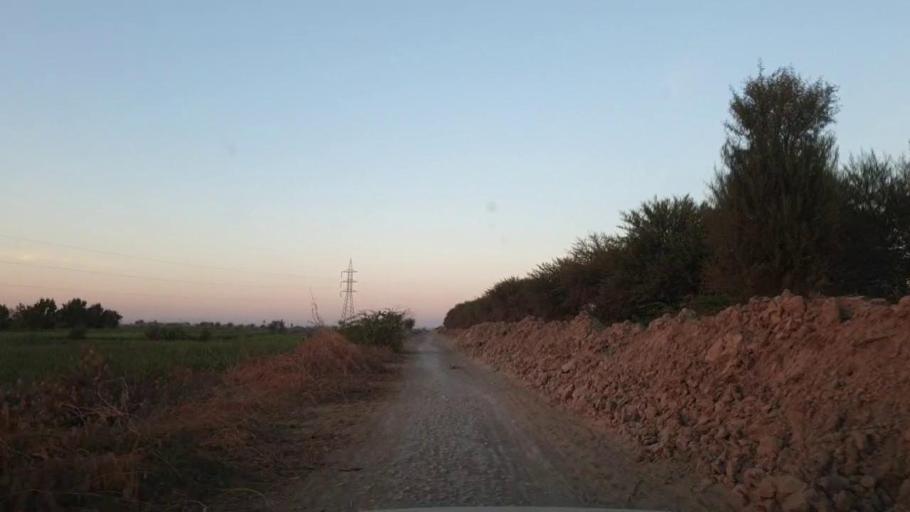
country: PK
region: Sindh
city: Kunri
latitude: 25.1512
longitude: 69.4467
